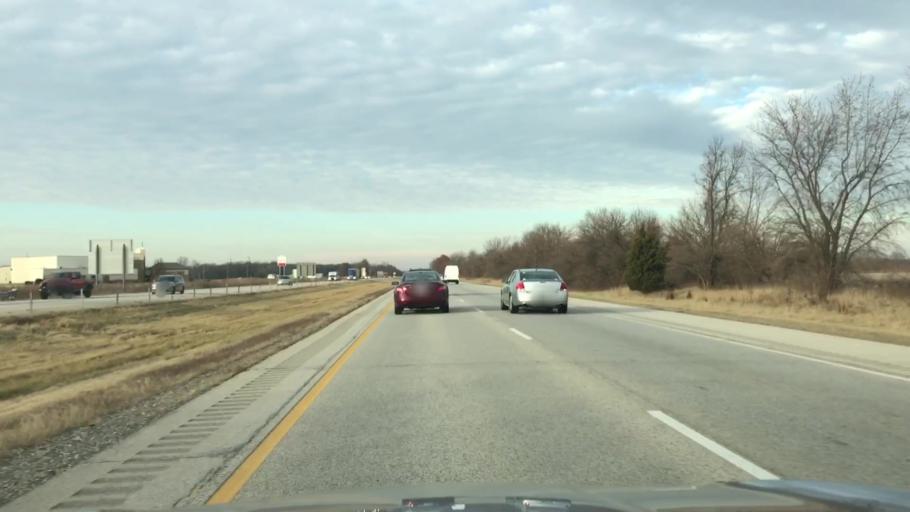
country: US
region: Illinois
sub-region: Sangamon County
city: Grandview
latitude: 39.8464
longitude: -89.5942
